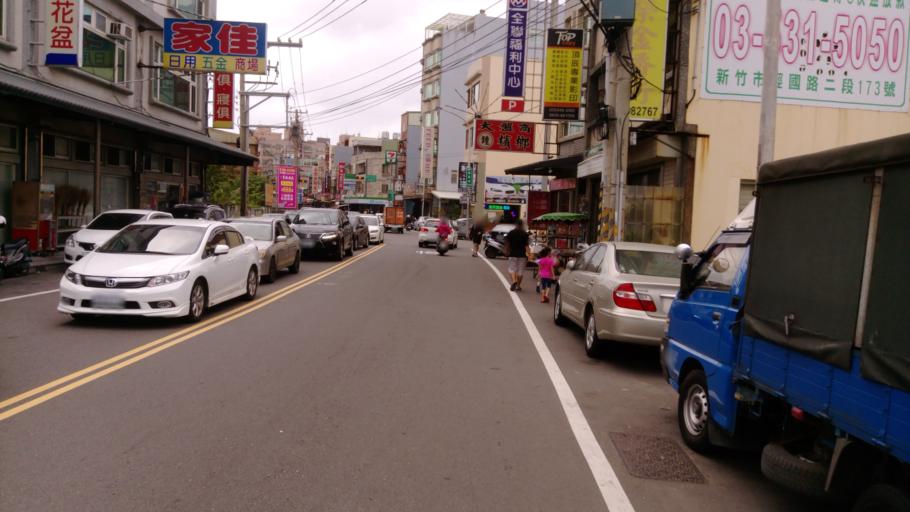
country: TW
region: Taiwan
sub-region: Hsinchu
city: Hsinchu
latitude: 24.7923
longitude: 120.9285
